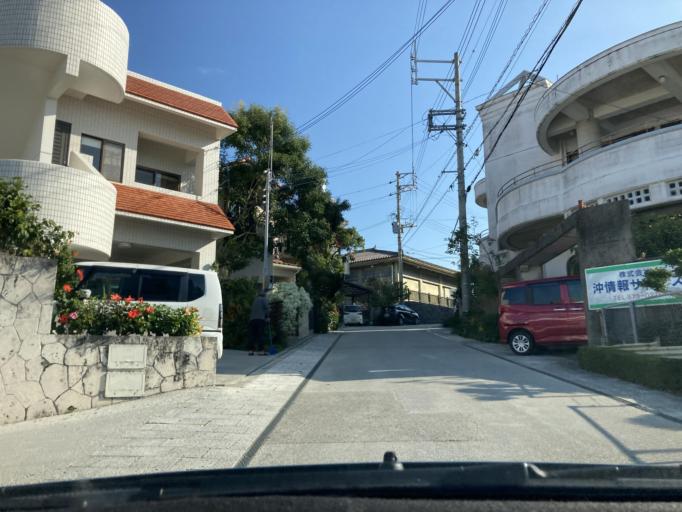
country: JP
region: Okinawa
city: Ginowan
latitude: 26.2485
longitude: 127.7283
